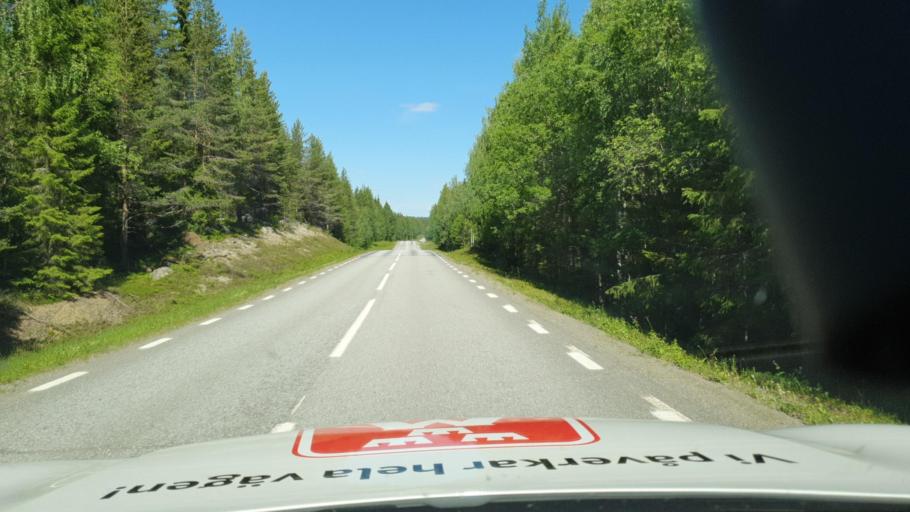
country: SE
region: Vaesterbotten
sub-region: Skelleftea Kommun
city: Boliden
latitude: 64.8303
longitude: 20.3717
